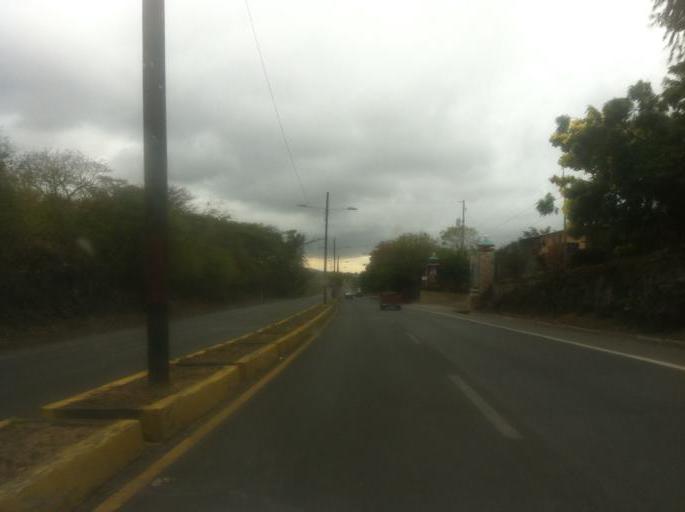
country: NI
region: Masaya
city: Nindiri
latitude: 12.0186
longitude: -86.1468
